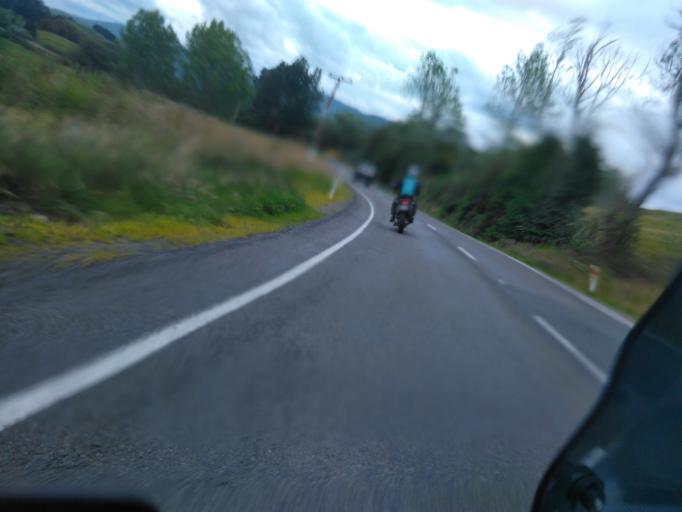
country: NZ
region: Bay of Plenty
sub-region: Opotiki District
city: Opotiki
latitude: -38.3872
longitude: 177.5552
